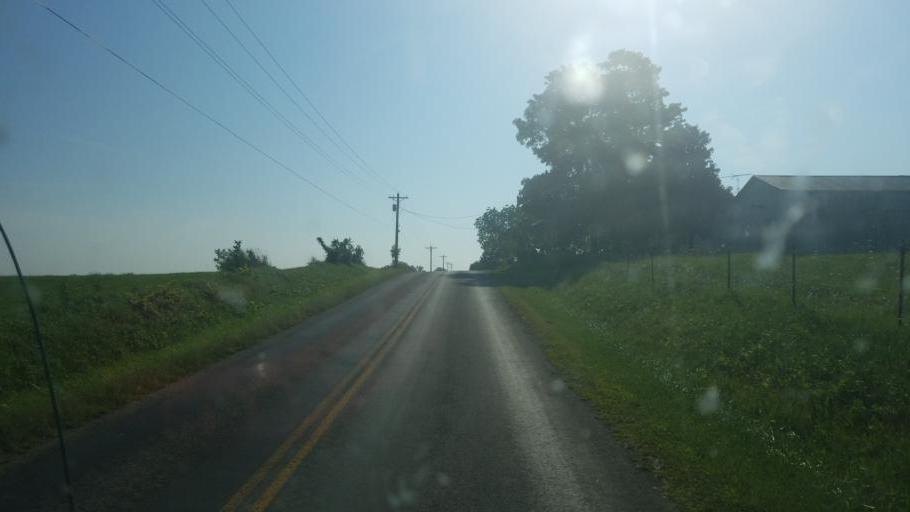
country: US
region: Ohio
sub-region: Huron County
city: New London
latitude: 41.0578
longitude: -82.2884
